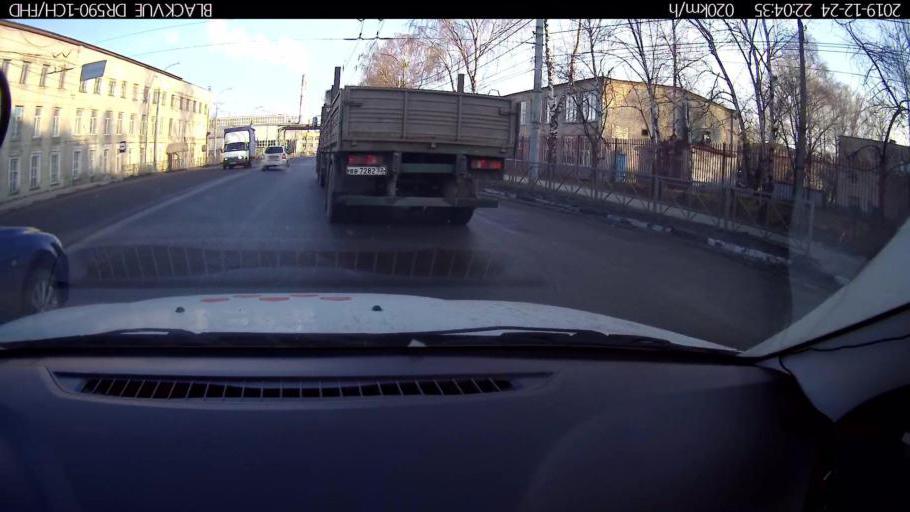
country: RU
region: Nizjnij Novgorod
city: Burevestnik
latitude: 56.2349
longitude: 43.8764
